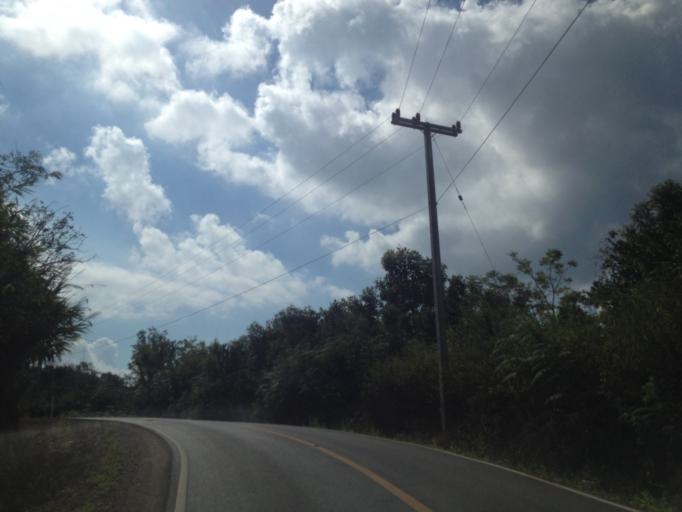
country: TH
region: Mae Hong Son
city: Ban Huai I Huak
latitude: 18.1446
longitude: 98.1355
